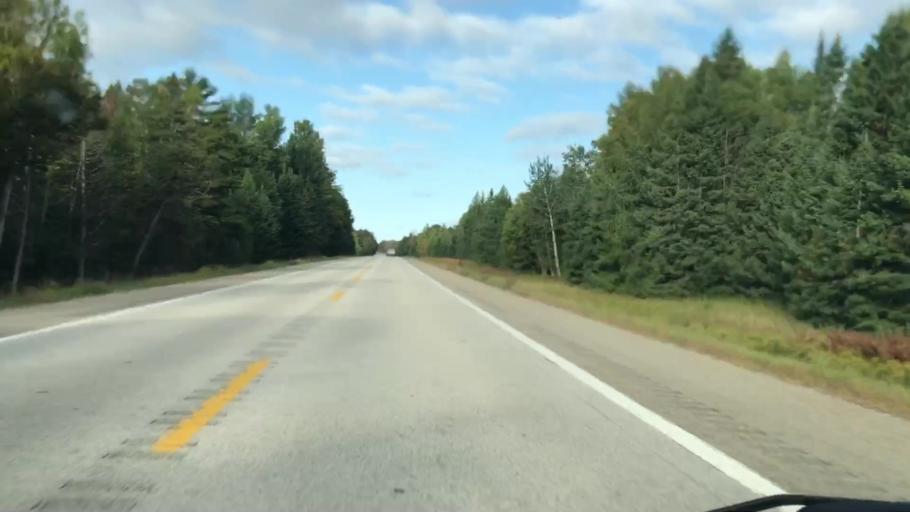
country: US
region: Michigan
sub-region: Luce County
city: Newberry
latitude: 46.3320
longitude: -85.0844
